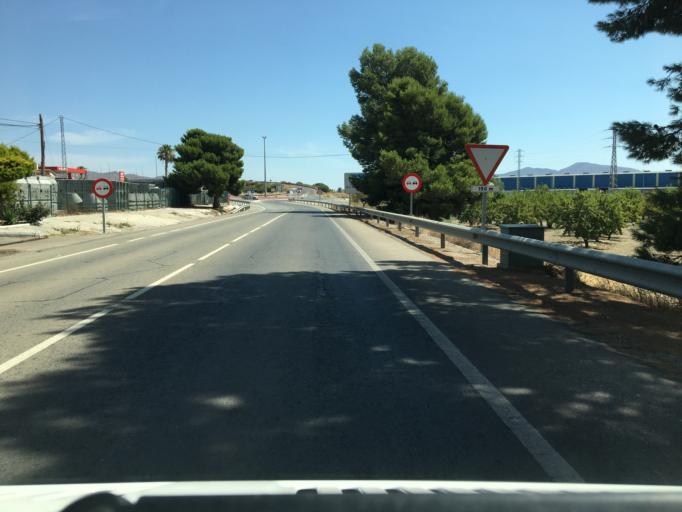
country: ES
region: Andalusia
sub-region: Provincia de Almeria
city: Huercal-Overa
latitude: 37.4327
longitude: -1.9109
